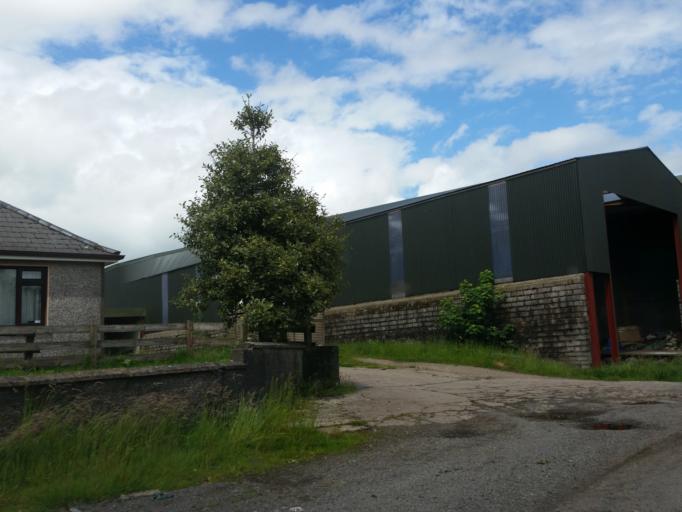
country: GB
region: Northern Ireland
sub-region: Omagh District
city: Omagh
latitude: 54.5467
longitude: -7.1371
